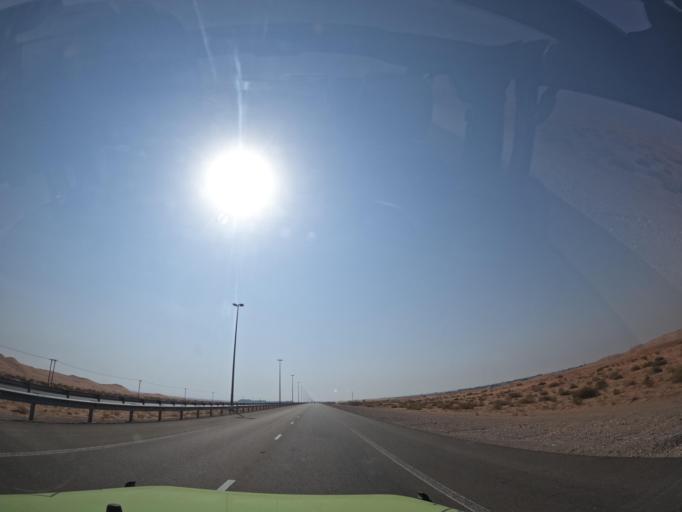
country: OM
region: Al Buraimi
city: Al Buraymi
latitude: 24.4279
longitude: 55.6803
